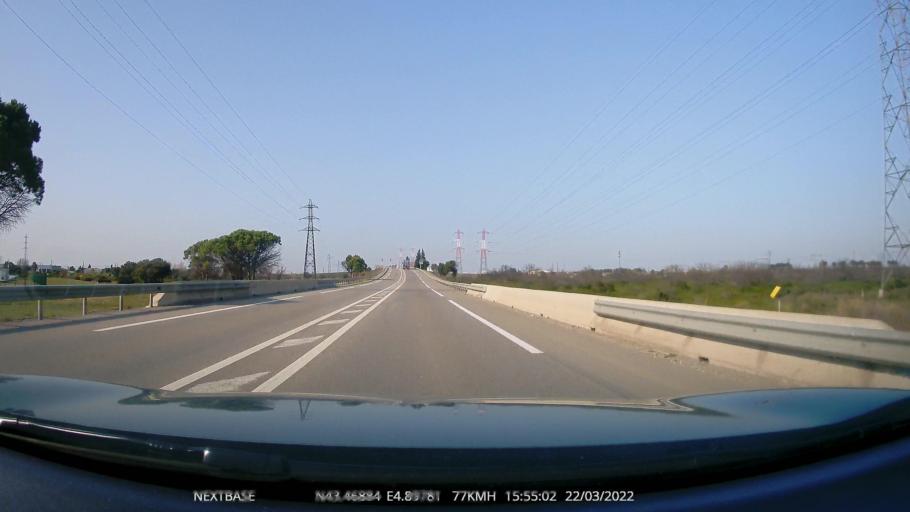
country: FR
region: Provence-Alpes-Cote d'Azur
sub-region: Departement des Bouches-du-Rhone
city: Fos-sur-Mer
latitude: 43.4692
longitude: 4.8978
